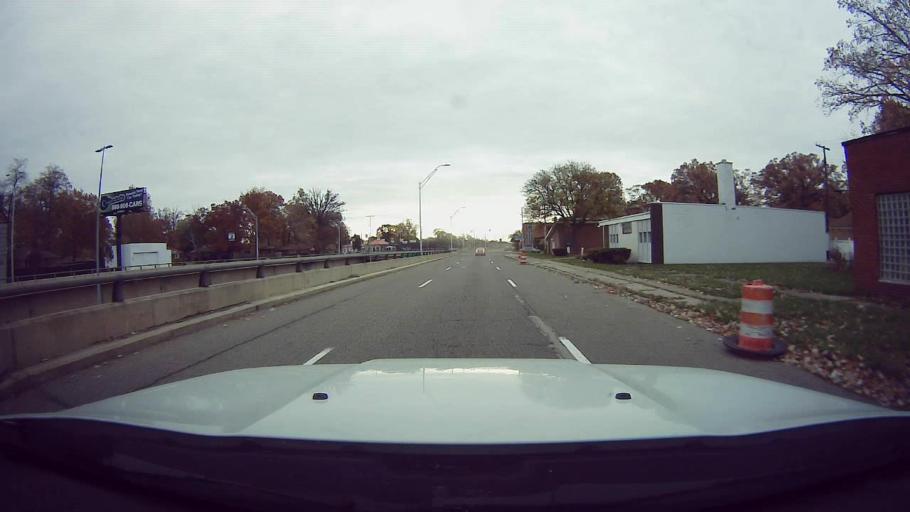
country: US
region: Michigan
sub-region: Oakland County
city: Oak Park
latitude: 42.4385
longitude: -83.1954
